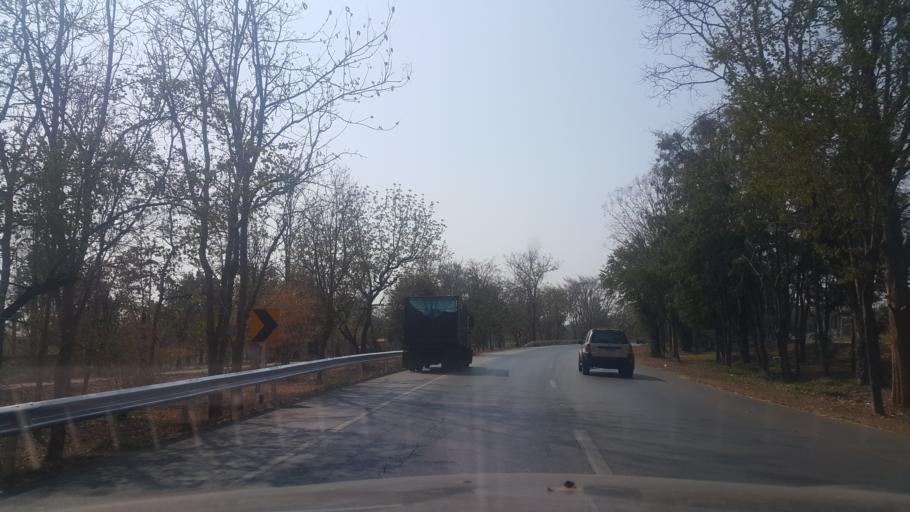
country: TH
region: Nakhon Ratchasima
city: Nakhon Ratchasima
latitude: 14.8704
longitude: 102.0727
